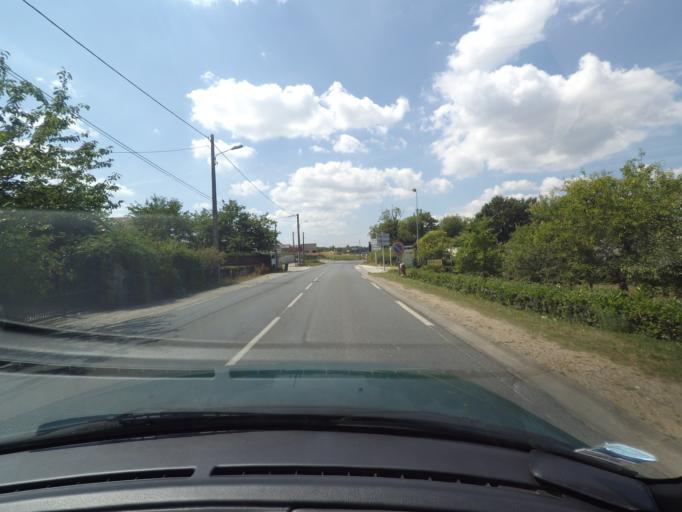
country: FR
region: Limousin
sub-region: Departement de la Haute-Vienne
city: Feytiat
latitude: 45.8122
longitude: 1.3028
